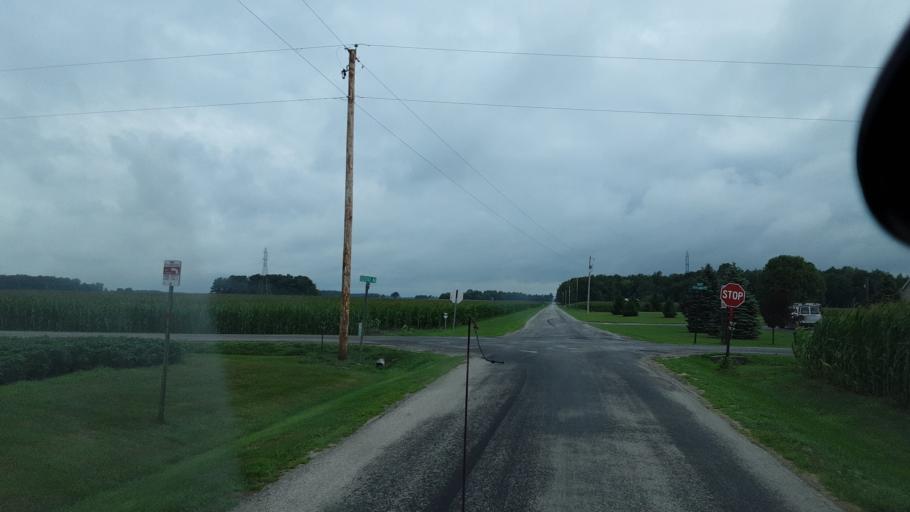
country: US
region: Indiana
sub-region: Allen County
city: Monroeville
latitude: 40.9213
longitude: -84.8427
